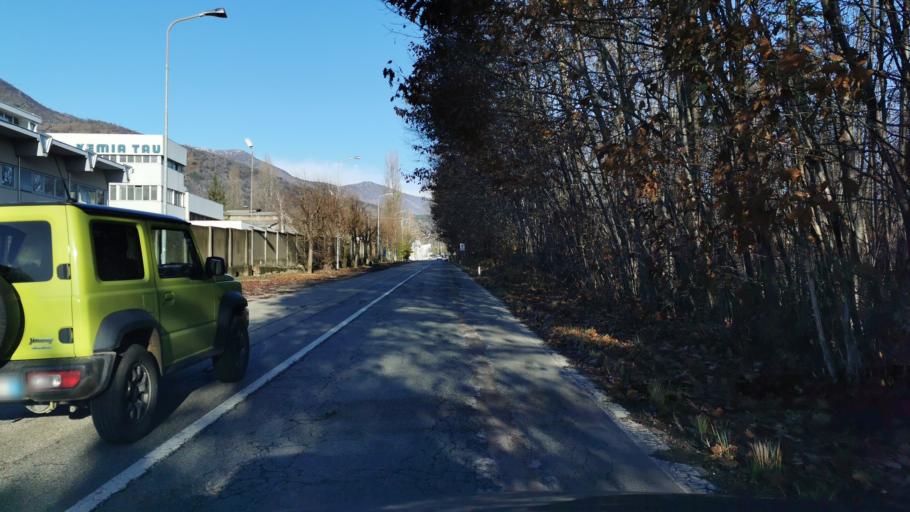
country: IT
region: Piedmont
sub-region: Provincia di Torino
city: La Cassa
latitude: 45.1706
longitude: 7.5215
